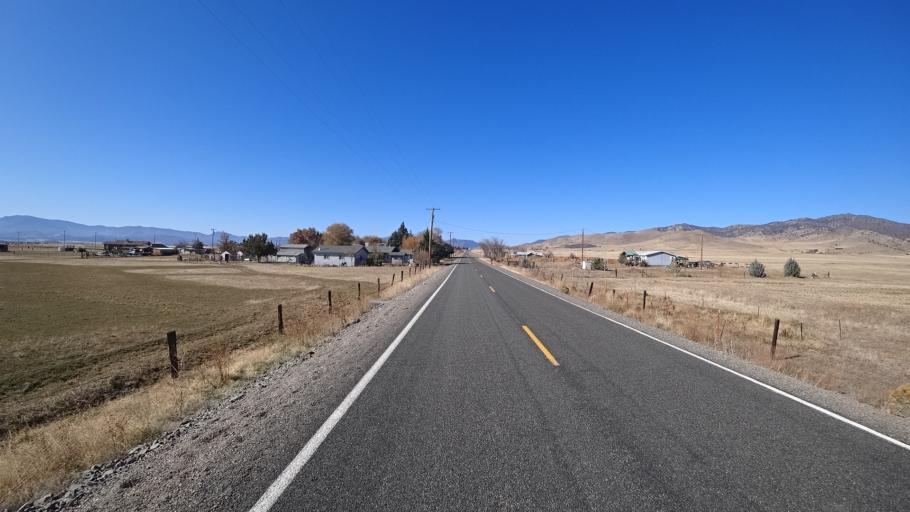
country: US
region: California
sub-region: Siskiyou County
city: Montague
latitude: 41.7705
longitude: -122.5027
